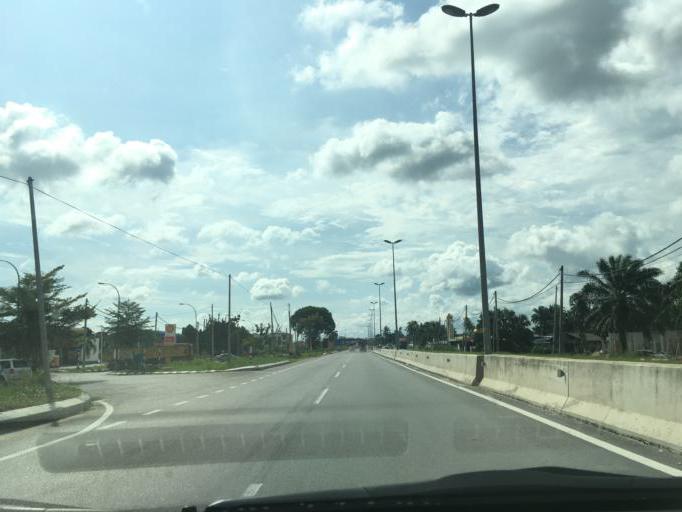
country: MY
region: Selangor
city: Batu Arang
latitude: 3.3120
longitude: 101.4199
